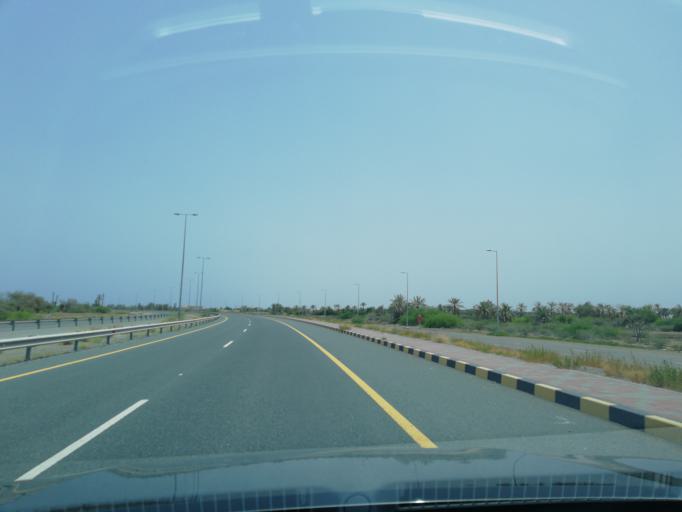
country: OM
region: Al Batinah
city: Shinas
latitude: 24.8364
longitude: 56.4263
